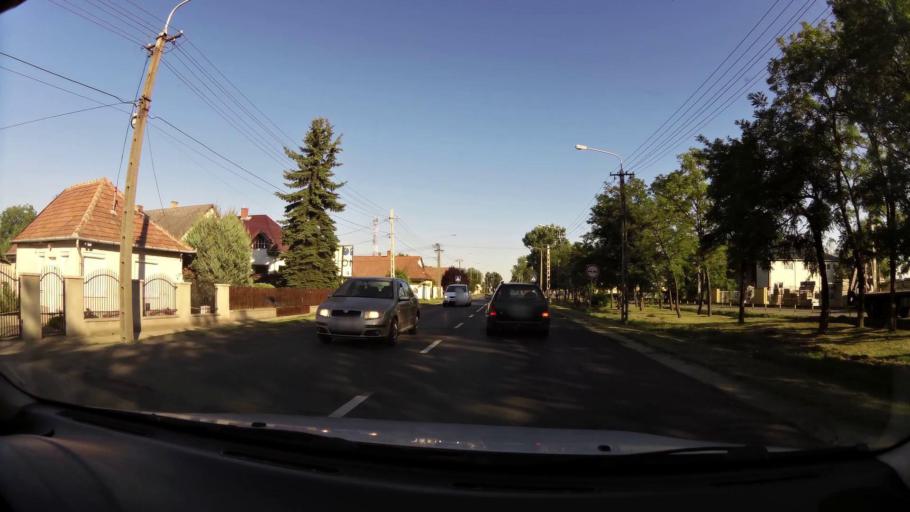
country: HU
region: Pest
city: Pilis
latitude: 47.2886
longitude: 19.5422
